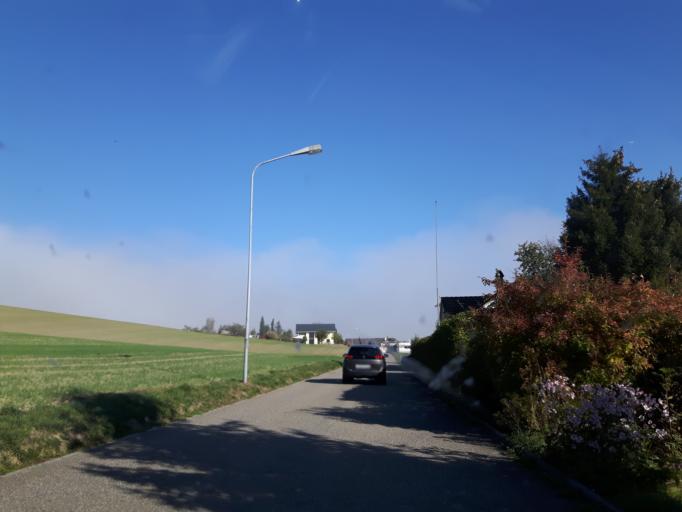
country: CH
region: Bern
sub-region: Oberaargau
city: Roggwil
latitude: 47.2304
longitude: 7.8296
